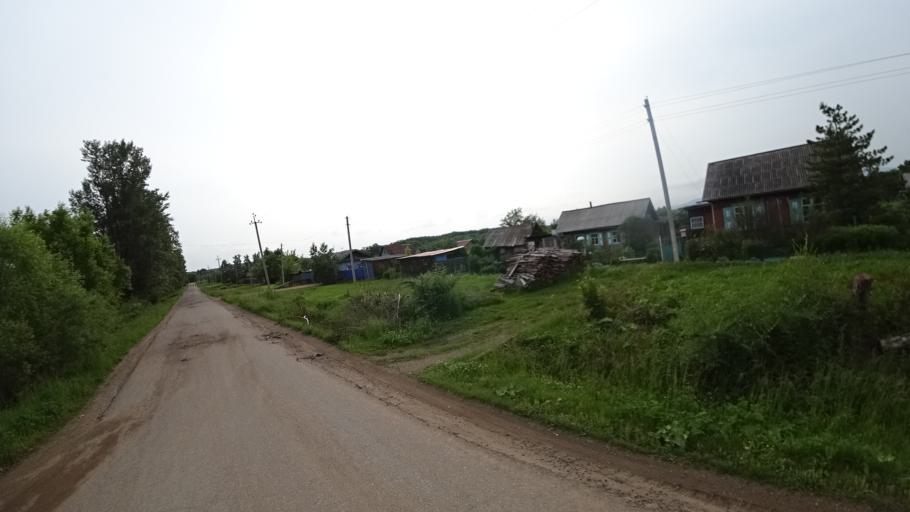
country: RU
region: Primorskiy
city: Novosysoyevka
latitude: 44.2482
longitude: 133.3772
